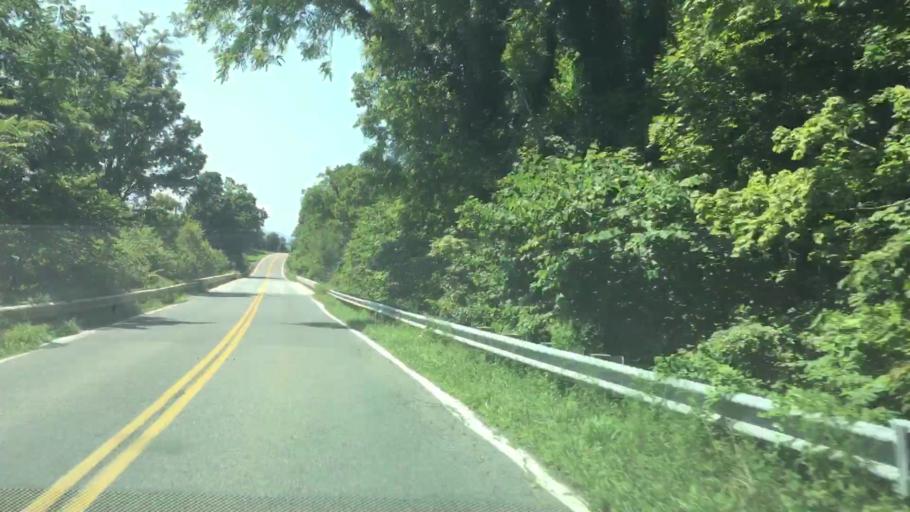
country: US
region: Virginia
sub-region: Washington County
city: Abingdon
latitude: 36.6059
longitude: -82.0351
